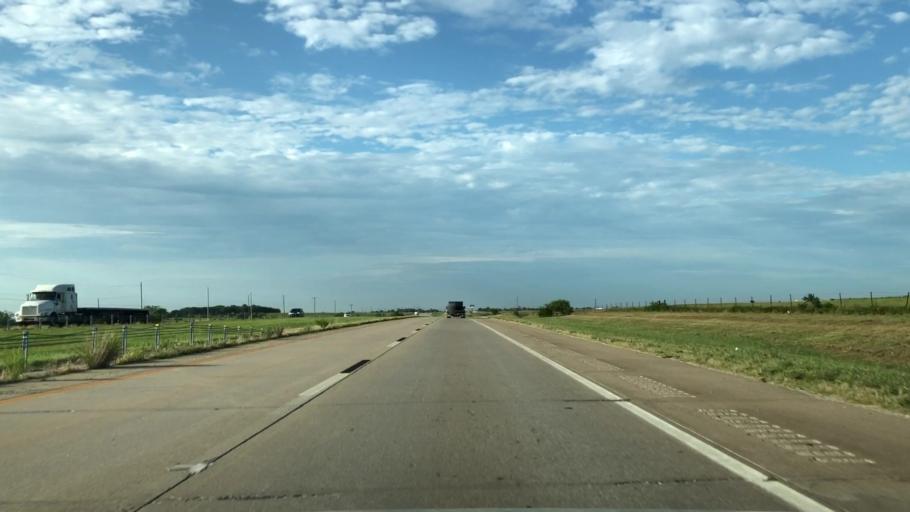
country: US
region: Oklahoma
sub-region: Osage County
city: Skiatook
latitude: 36.3912
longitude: -95.9206
